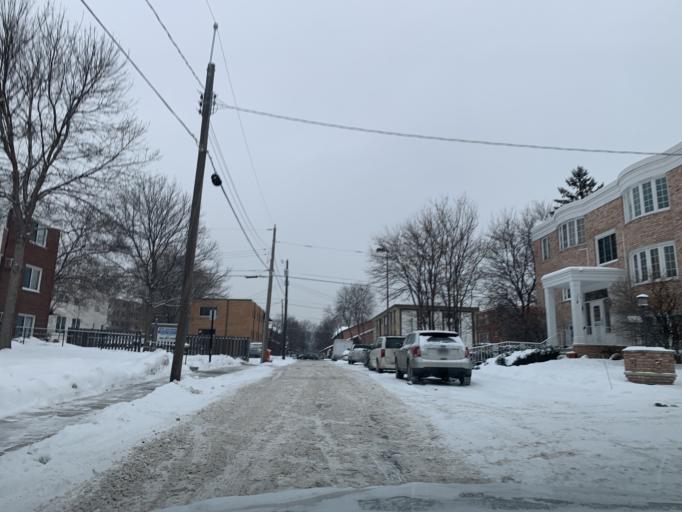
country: US
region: Minnesota
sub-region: Hennepin County
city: Saint Louis Park
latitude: 44.9474
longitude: -93.3361
